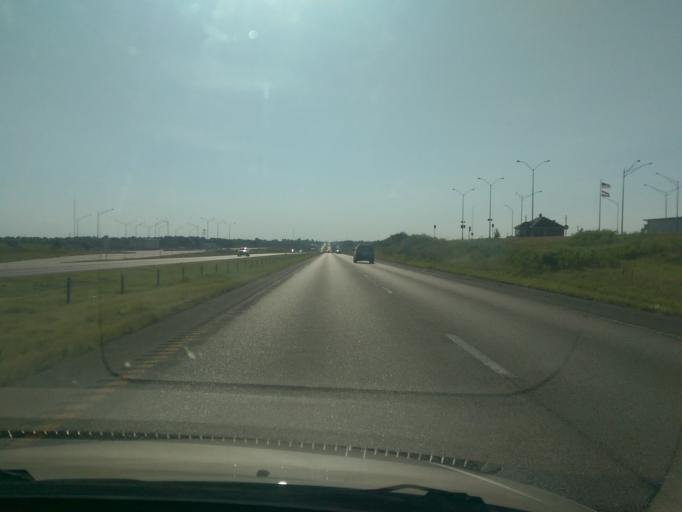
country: US
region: Missouri
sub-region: Lafayette County
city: Odessa
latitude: 39.0043
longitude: -93.8497
